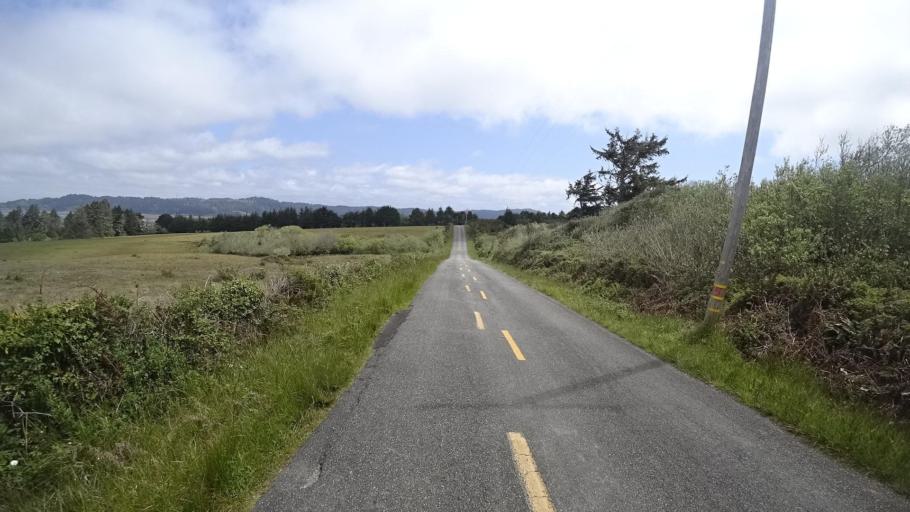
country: US
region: California
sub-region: Humboldt County
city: Humboldt Hill
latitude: 40.6869
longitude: -124.2444
